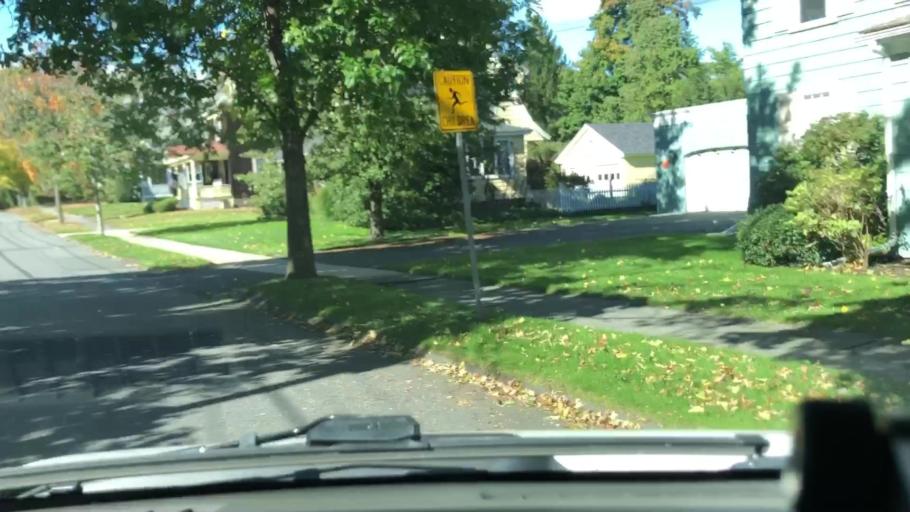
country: US
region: Massachusetts
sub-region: Franklin County
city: Greenfield
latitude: 42.5972
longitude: -72.5896
